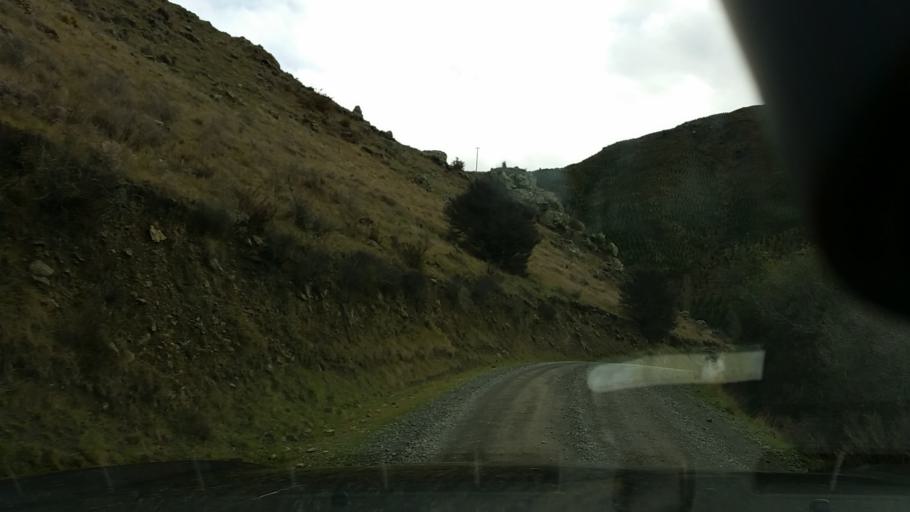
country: NZ
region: Tasman
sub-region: Tasman District
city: Richmond
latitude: -41.7305
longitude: 173.4468
